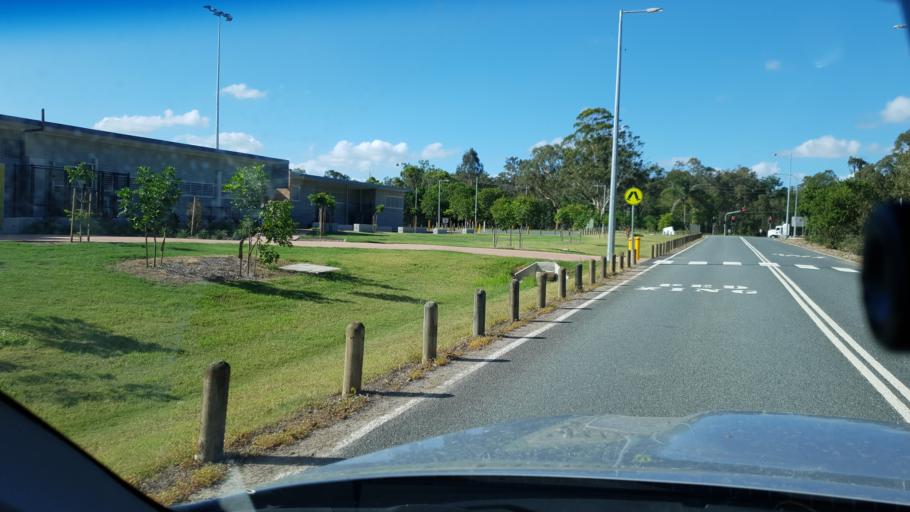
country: AU
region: Queensland
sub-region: Logan
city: Woodridge
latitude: -27.6710
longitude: 153.0706
